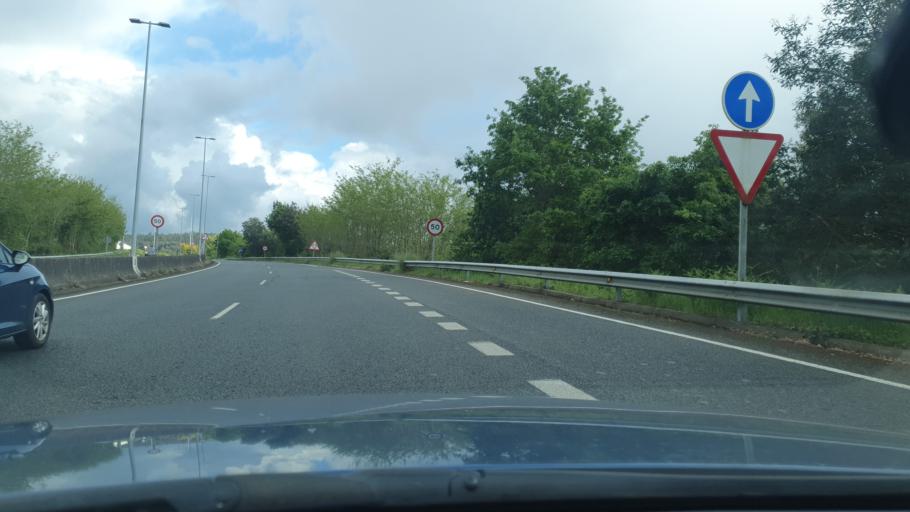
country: ES
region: Galicia
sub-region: Provincia da Coruna
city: Santiago de Compostela
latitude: 42.8656
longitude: -8.5704
